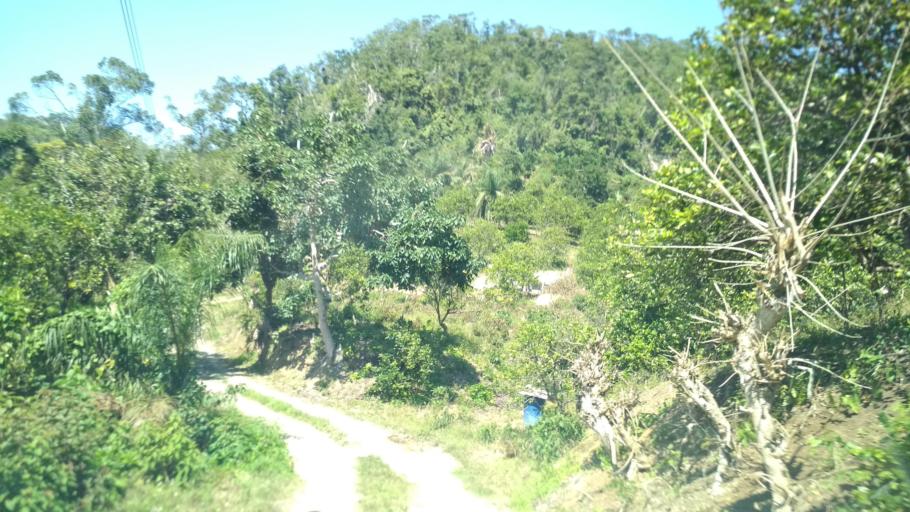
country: MX
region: Veracruz
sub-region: Papantla
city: Polutla
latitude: 20.4890
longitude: -97.2298
